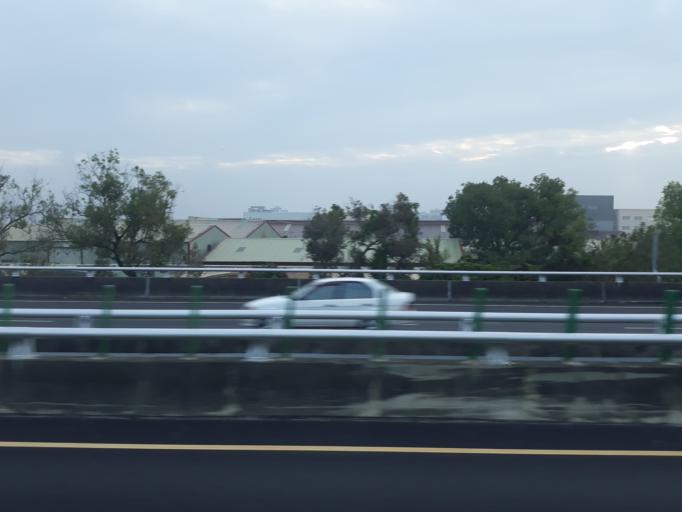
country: TW
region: Taiwan
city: Fengyuan
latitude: 24.2791
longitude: 120.6938
